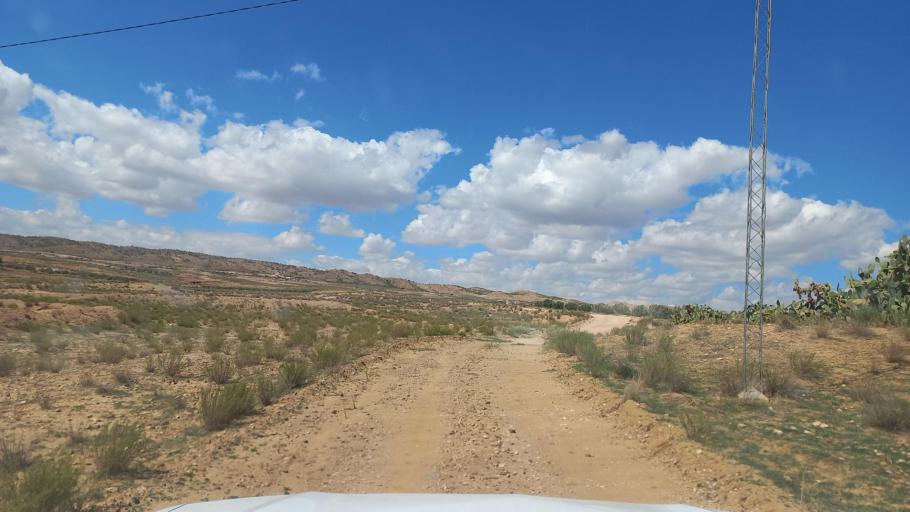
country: TN
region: Al Qasrayn
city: Sbiba
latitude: 35.3539
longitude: 9.0122
